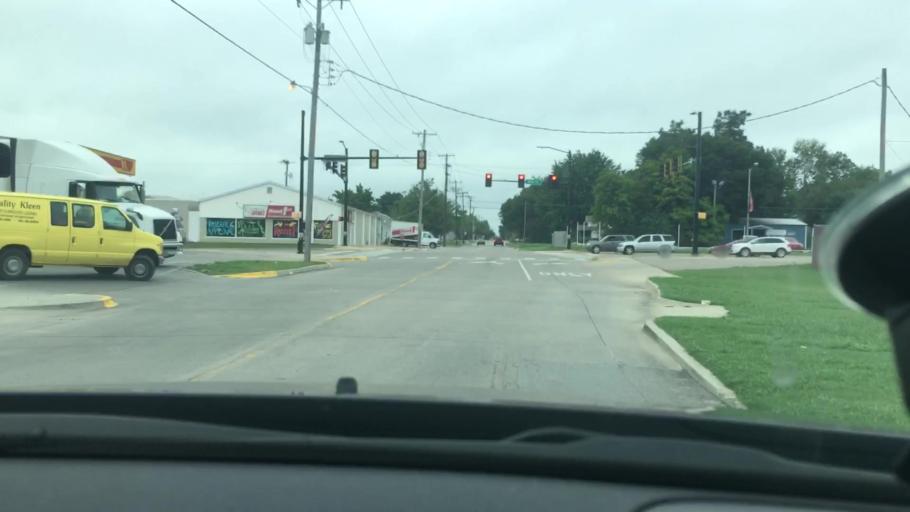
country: US
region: Oklahoma
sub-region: Pontotoc County
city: Ada
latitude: 34.7752
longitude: -96.6867
